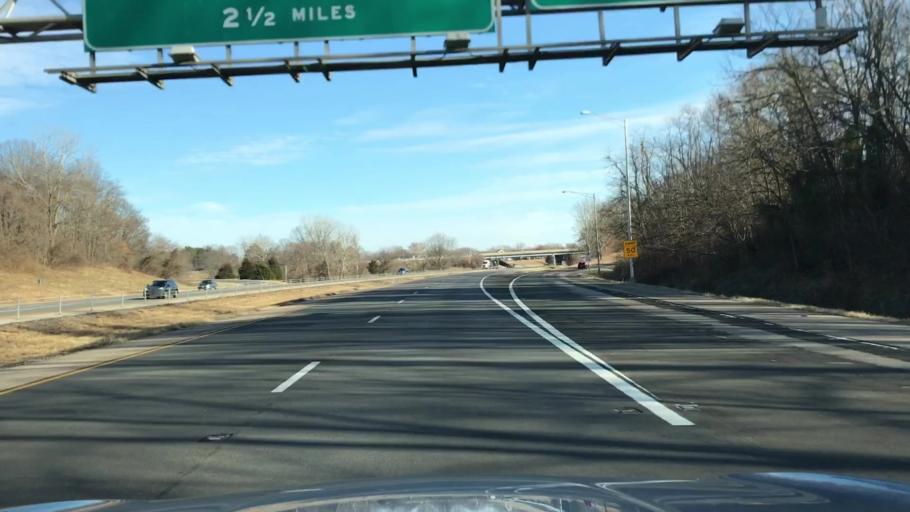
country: US
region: Illinois
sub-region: Madison County
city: Glen Carbon
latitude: 38.7567
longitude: -89.9614
